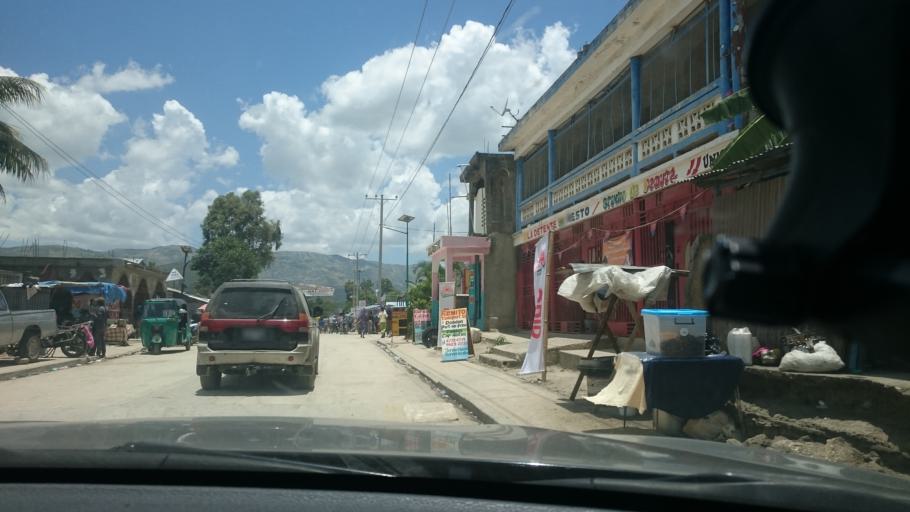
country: HT
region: Nord
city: Dondon
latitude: 19.5309
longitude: -72.2410
